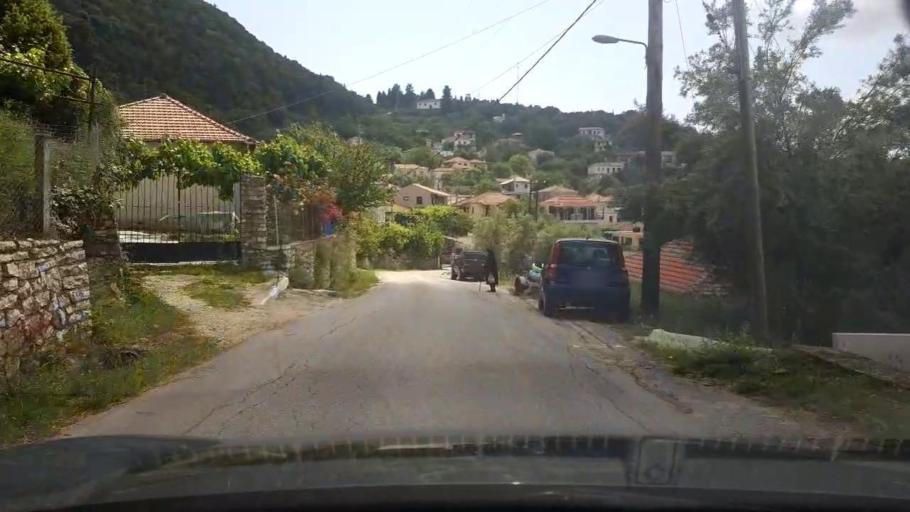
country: GR
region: Ionian Islands
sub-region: Lefkada
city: Nidri
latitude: 38.6437
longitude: 20.7071
